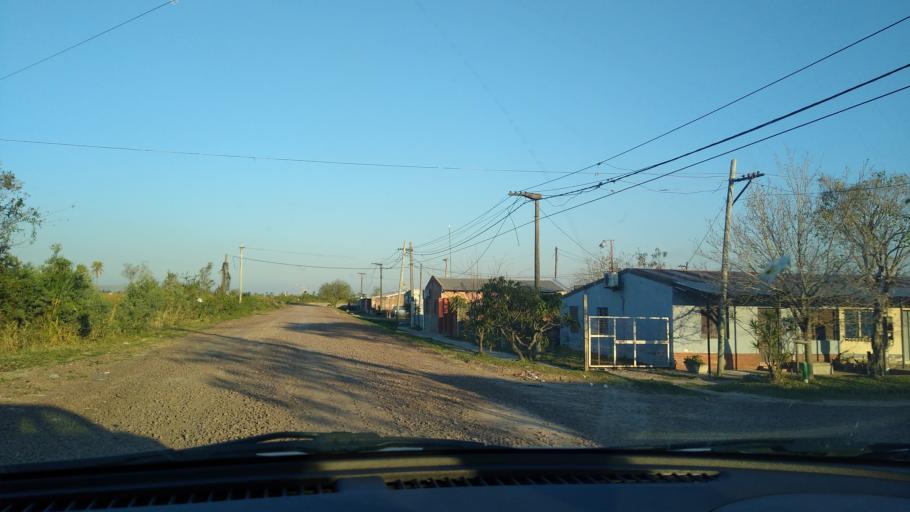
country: AR
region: Chaco
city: Puerto Vilelas
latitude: -27.5044
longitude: -58.9552
